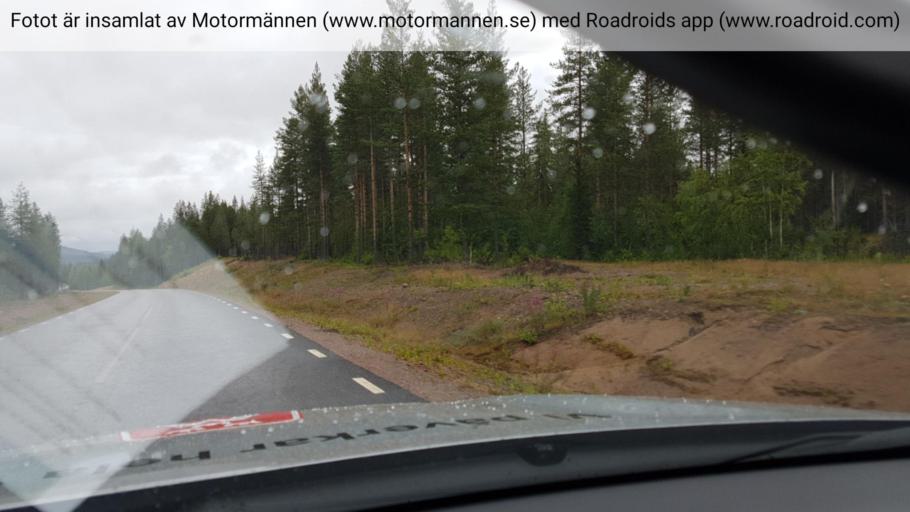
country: SE
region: Norrbotten
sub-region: Gallivare Kommun
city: Gaellivare
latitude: 66.6166
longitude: 20.4333
